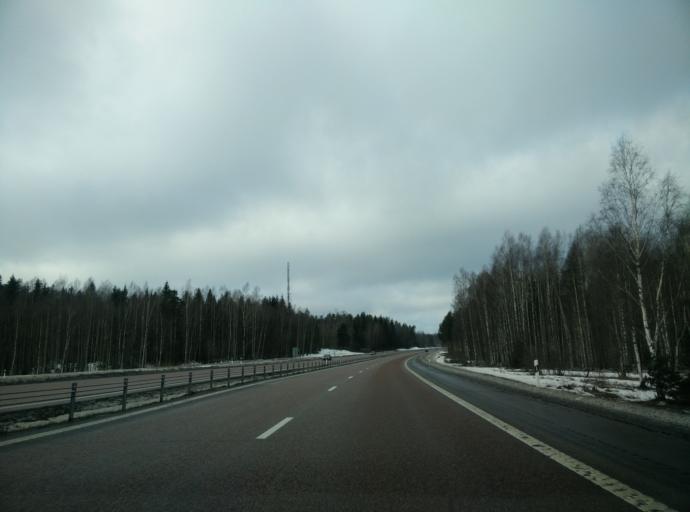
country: SE
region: Gaevleborg
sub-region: Sandvikens Kommun
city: Sandviken
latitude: 60.6249
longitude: 16.8943
